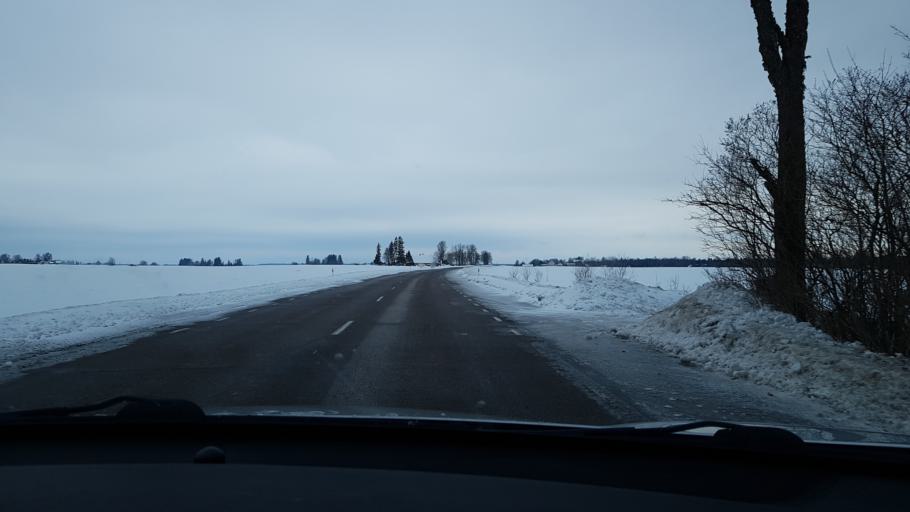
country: EE
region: Jaervamaa
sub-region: Jaerva-Jaani vald
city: Jarva-Jaani
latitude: 58.9140
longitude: 25.8601
